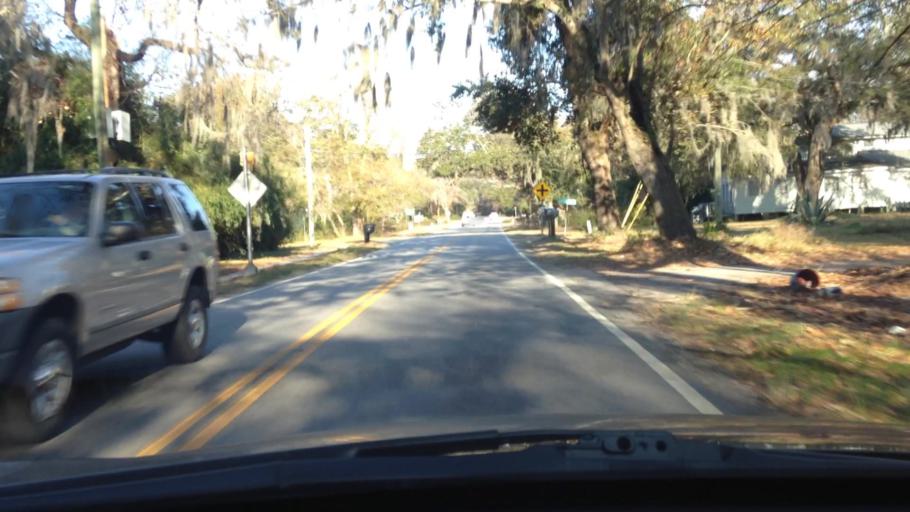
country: US
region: South Carolina
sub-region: Charleston County
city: Charleston
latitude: 32.7461
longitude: -79.9867
